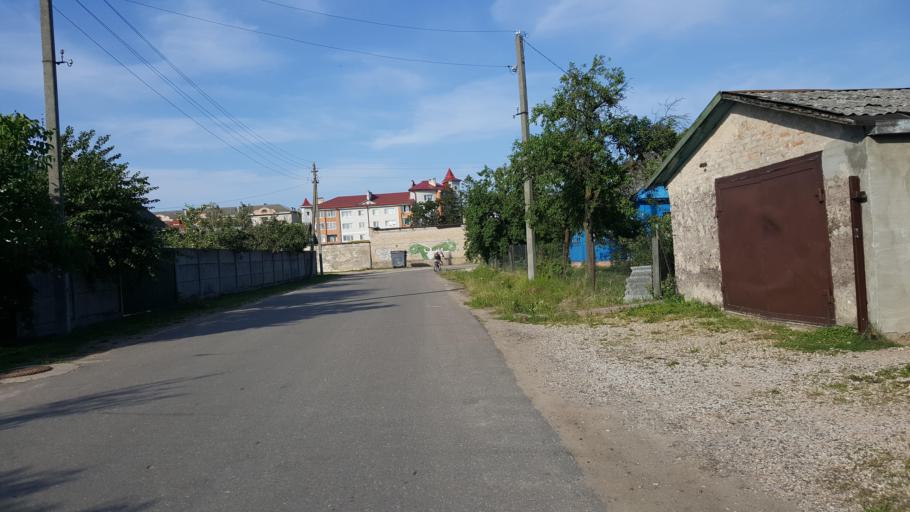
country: BY
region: Brest
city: Vysokaye
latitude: 52.3764
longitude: 23.3653
